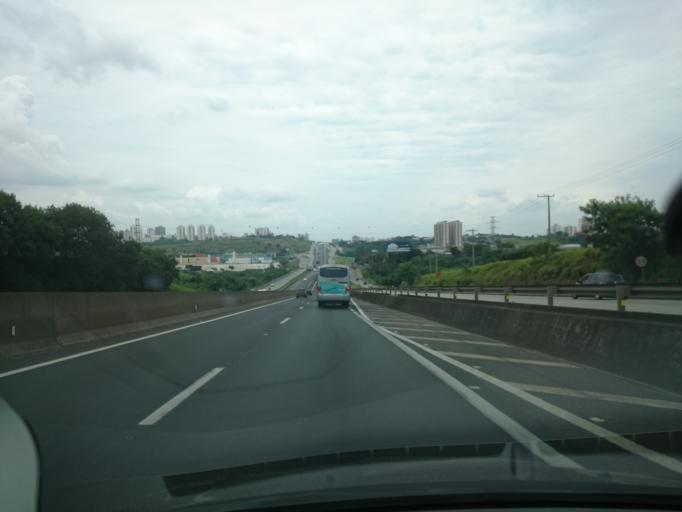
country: BR
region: Sao Paulo
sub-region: Votorantim
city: Votorantim
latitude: -23.5253
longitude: -47.4428
